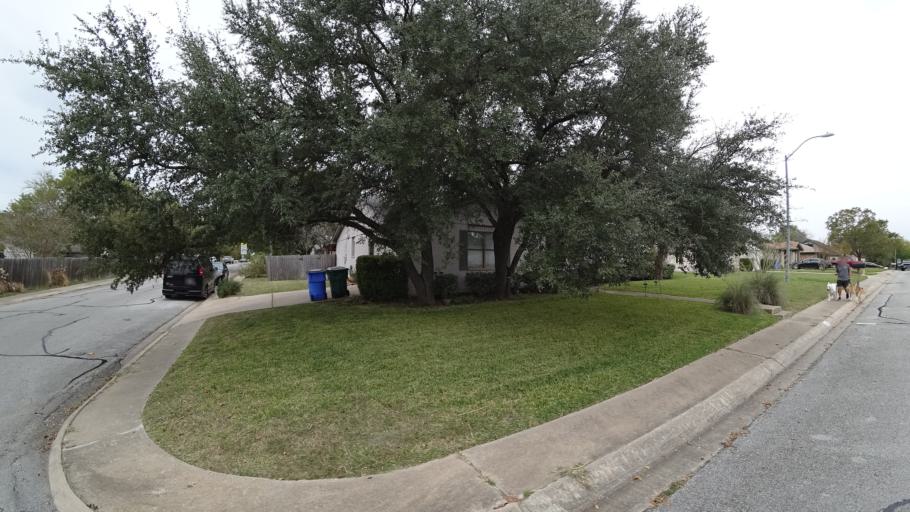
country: US
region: Texas
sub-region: Travis County
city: Pflugerville
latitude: 30.4290
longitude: -97.6110
